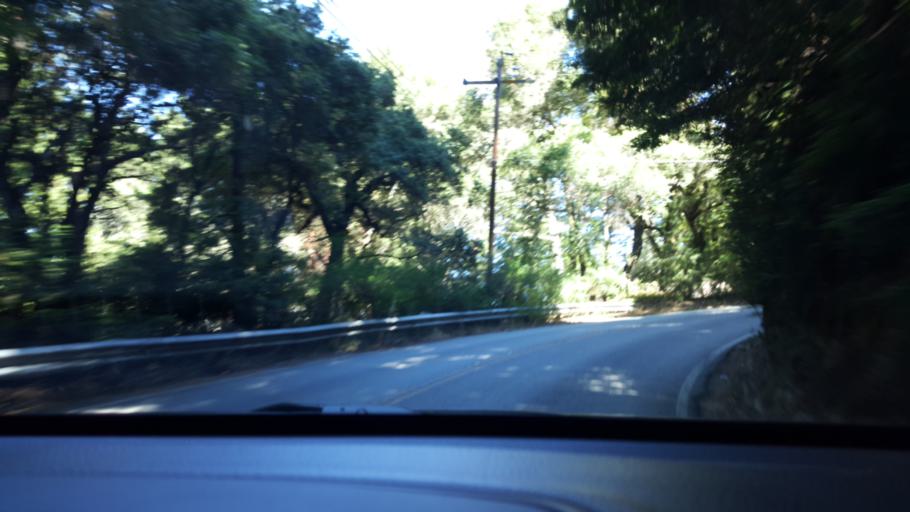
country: US
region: California
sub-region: San Mateo County
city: Portola Valley
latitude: 37.3862
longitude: -122.2616
